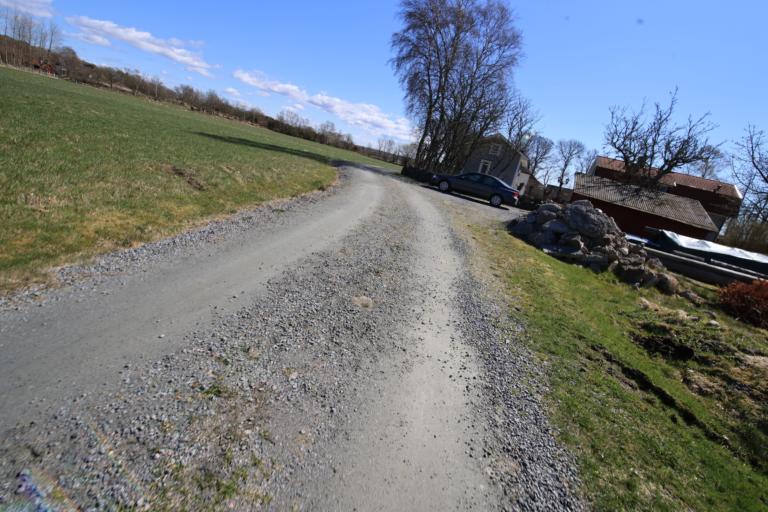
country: SE
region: Halland
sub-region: Varbergs Kommun
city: Varberg
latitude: 57.1609
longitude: 12.2518
